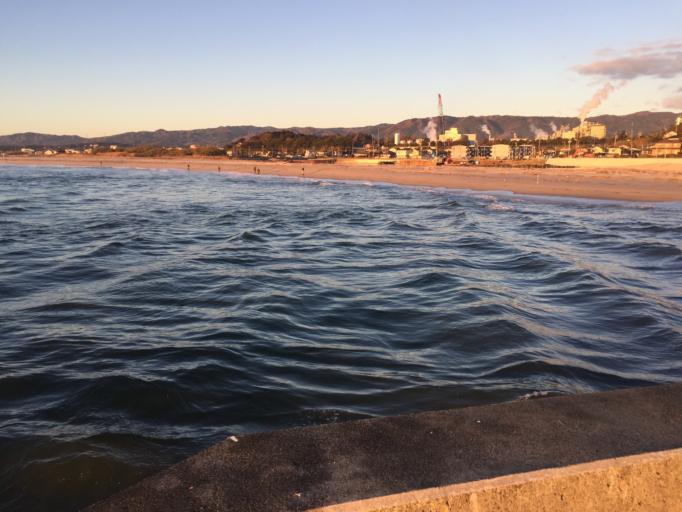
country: JP
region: Ibaraki
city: Kitaibaraki
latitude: 36.7944
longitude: 140.7568
